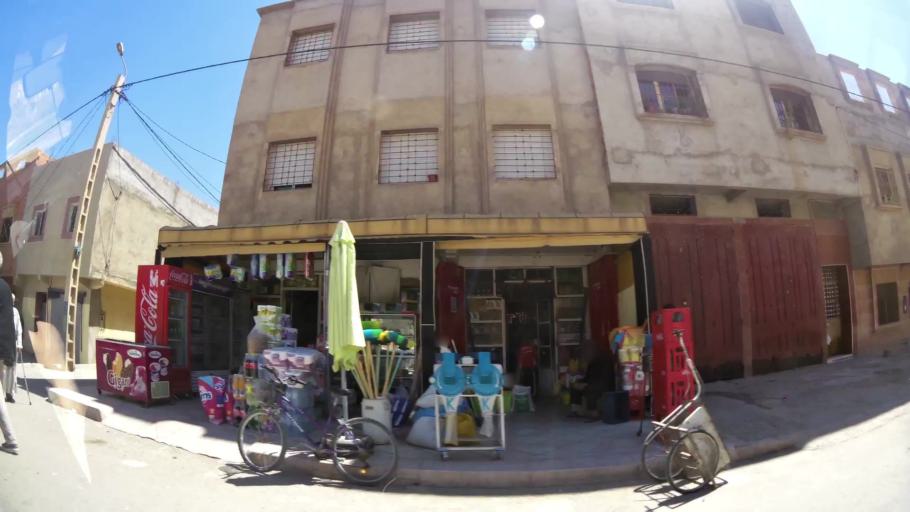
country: MA
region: Oriental
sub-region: Oujda-Angad
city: Oujda
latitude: 34.6615
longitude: -1.8811
